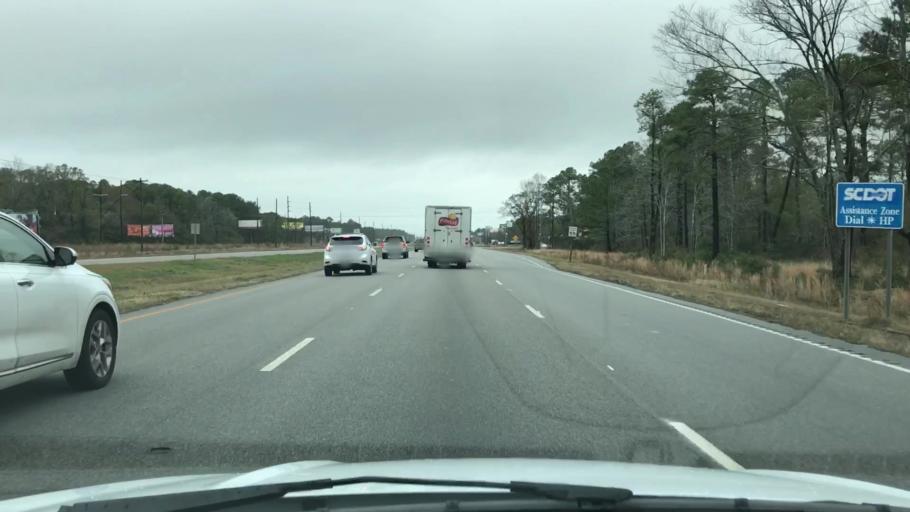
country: US
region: South Carolina
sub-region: Horry County
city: Forestbrook
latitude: 33.7699
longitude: -78.9780
